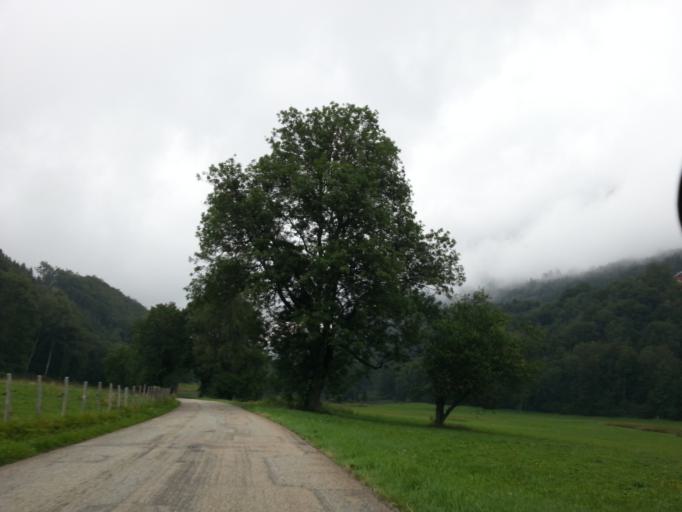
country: FR
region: Rhone-Alpes
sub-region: Departement de la Savoie
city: Mercury
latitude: 45.6751
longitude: 6.3088
